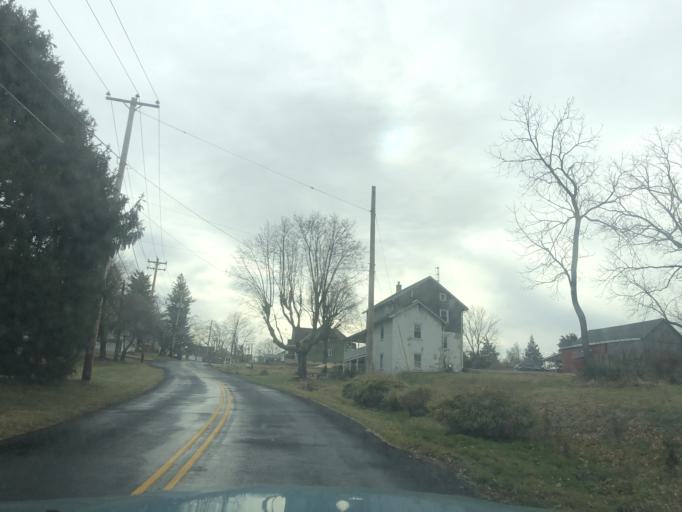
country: US
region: Pennsylvania
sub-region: Montgomery County
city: Harleysville
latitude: 40.2651
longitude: -75.4076
